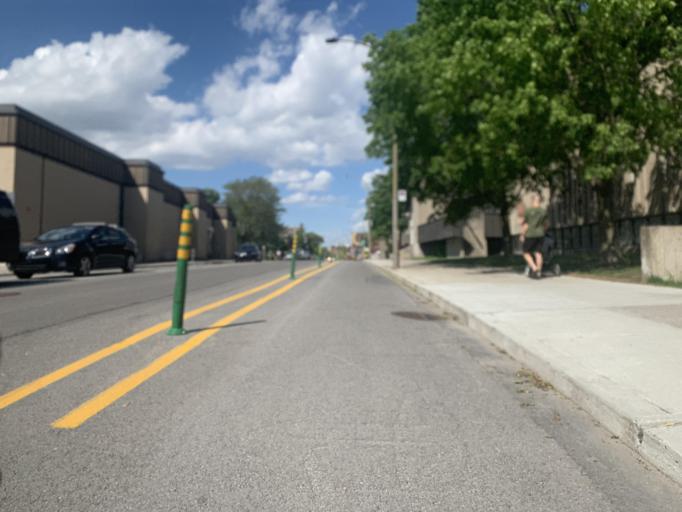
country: CA
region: Quebec
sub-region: Montreal
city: Montreal
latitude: 45.5403
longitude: -73.5945
